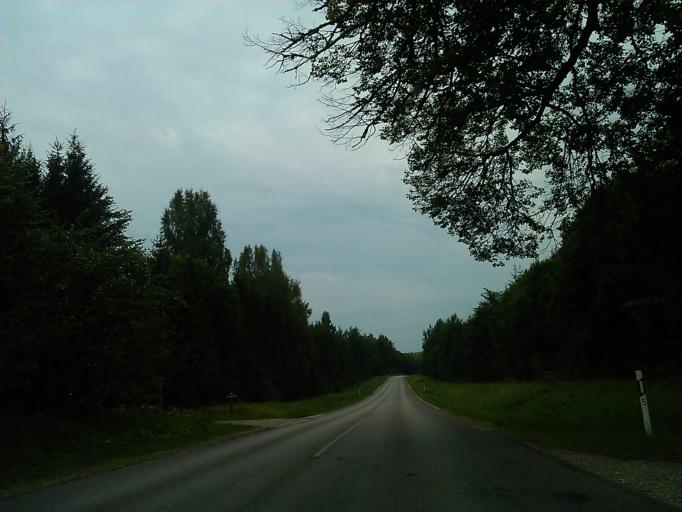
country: LV
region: Beverina
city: Murmuiza
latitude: 57.4423
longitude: 25.4353
